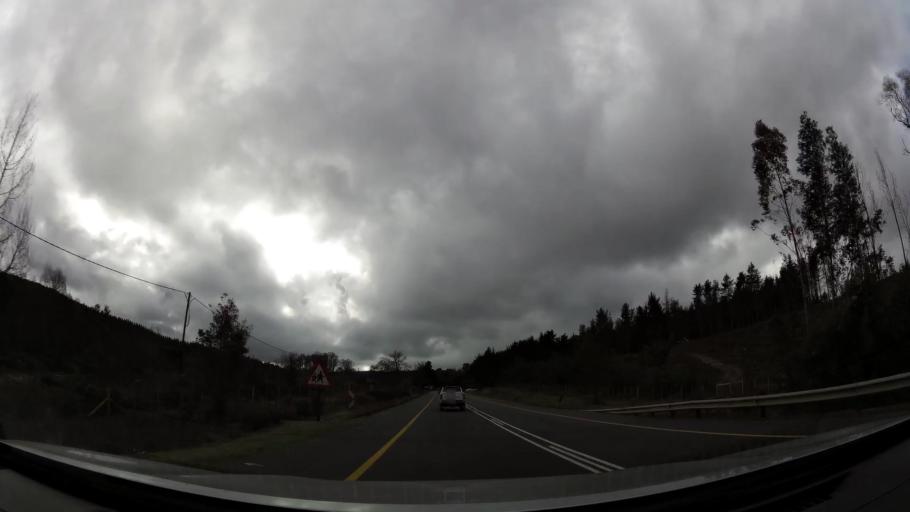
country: ZA
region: Western Cape
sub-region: Eden District Municipality
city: Knysna
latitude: -34.0311
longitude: 23.1589
